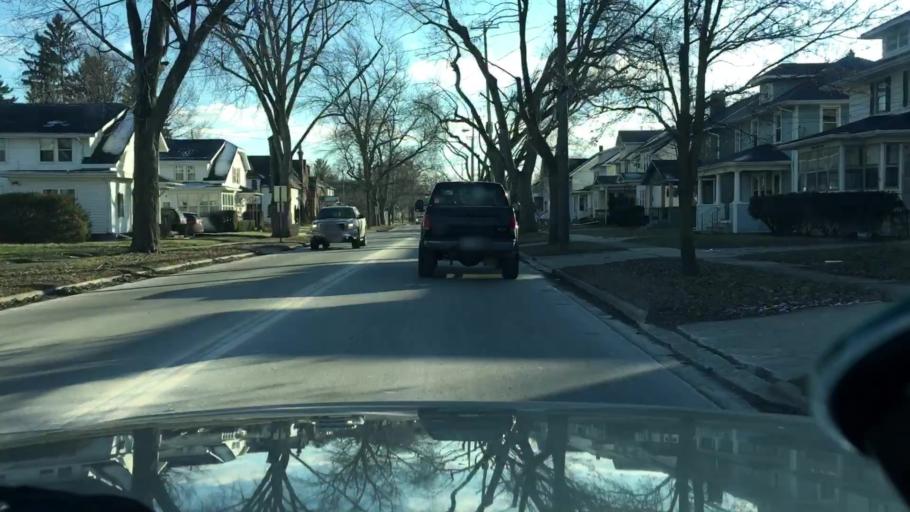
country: US
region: Michigan
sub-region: Jackson County
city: Jackson
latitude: 42.2416
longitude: -84.4234
